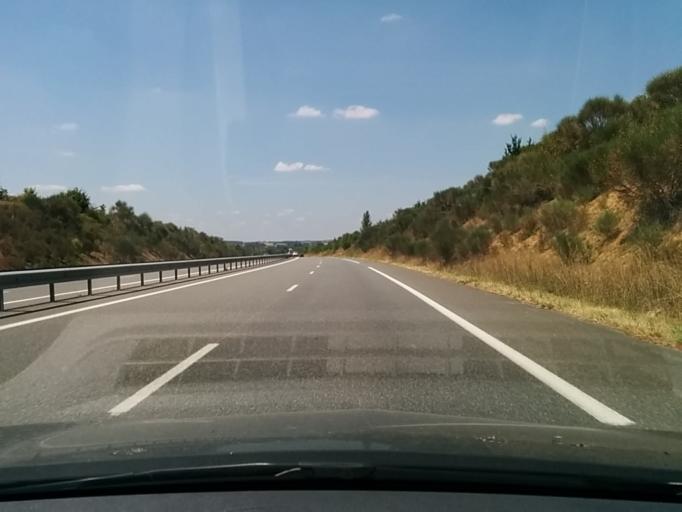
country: FR
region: Midi-Pyrenees
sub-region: Departement du Gers
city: Aubiet
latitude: 43.6409
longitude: 0.8160
